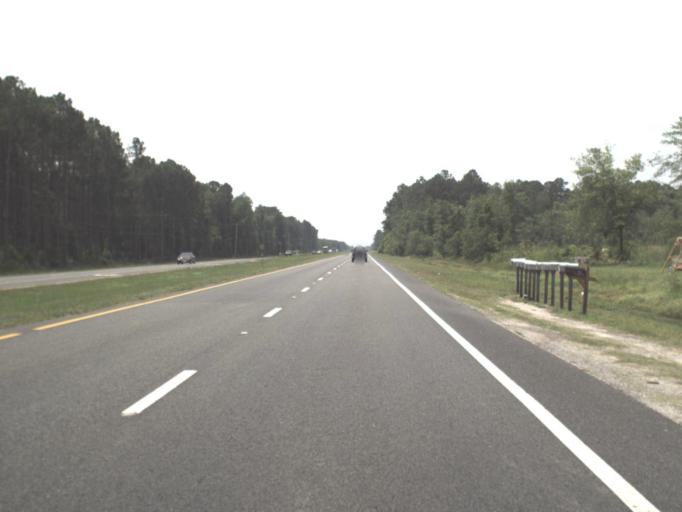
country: US
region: Florida
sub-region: Clay County
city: Green Cove Springs
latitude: 29.8520
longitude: -81.6627
